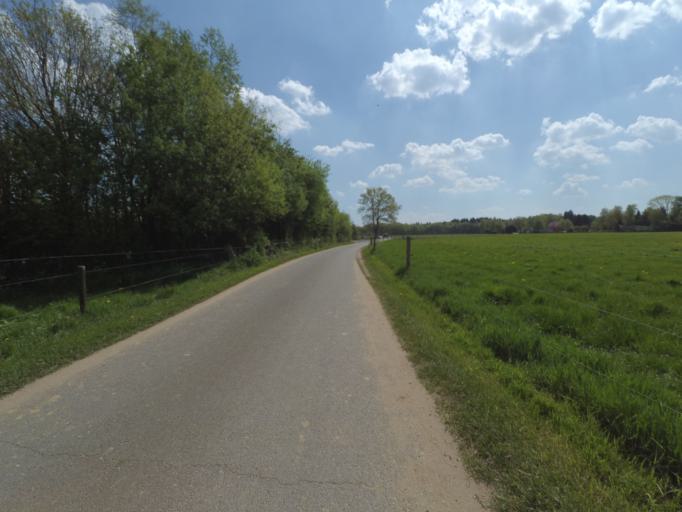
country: NL
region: Gelderland
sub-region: Gemeente Barneveld
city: Garderen
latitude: 52.2279
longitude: 5.7250
